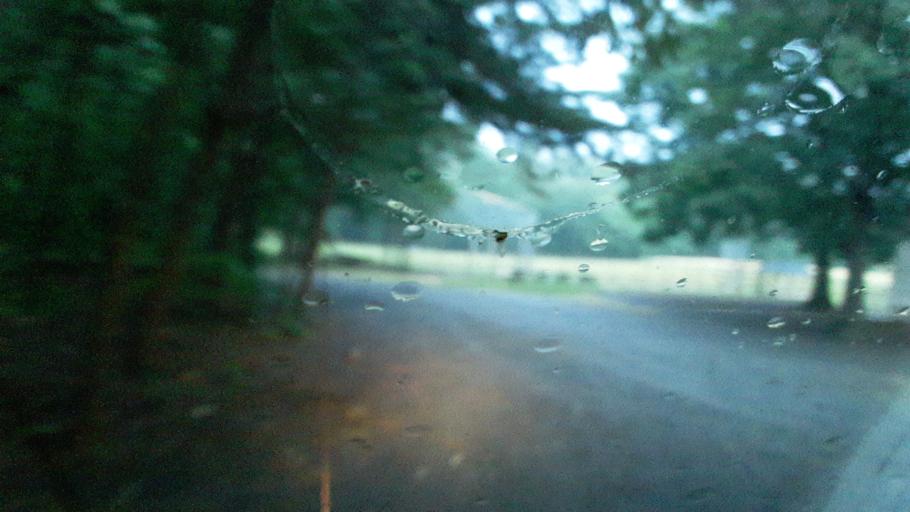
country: US
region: North Carolina
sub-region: Yadkin County
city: Jonesville
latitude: 36.0771
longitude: -80.8563
